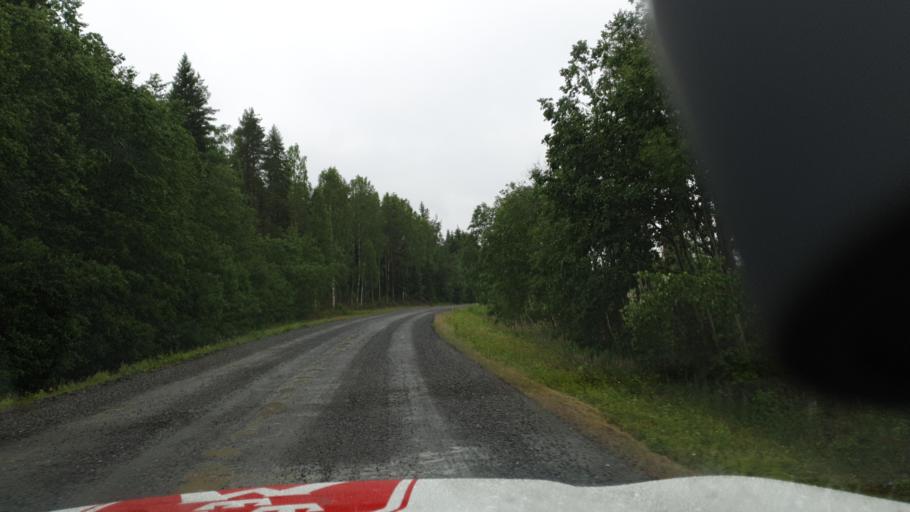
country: SE
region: Vaesterbotten
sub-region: Nordmalings Kommun
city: Nordmaling
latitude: 63.7122
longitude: 19.6334
